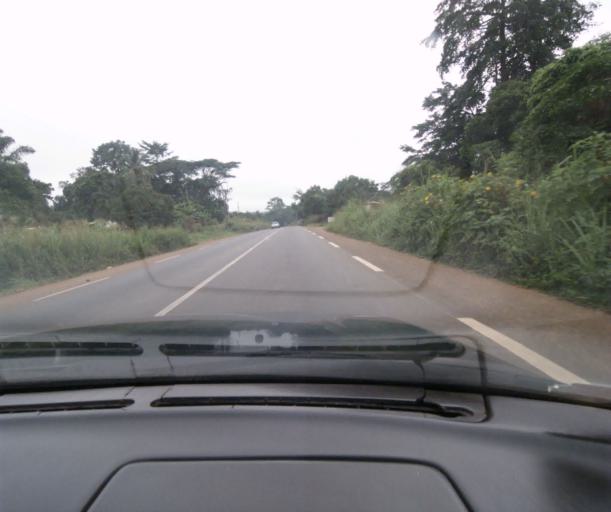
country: CM
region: Centre
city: Obala
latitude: 4.1932
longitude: 11.4530
